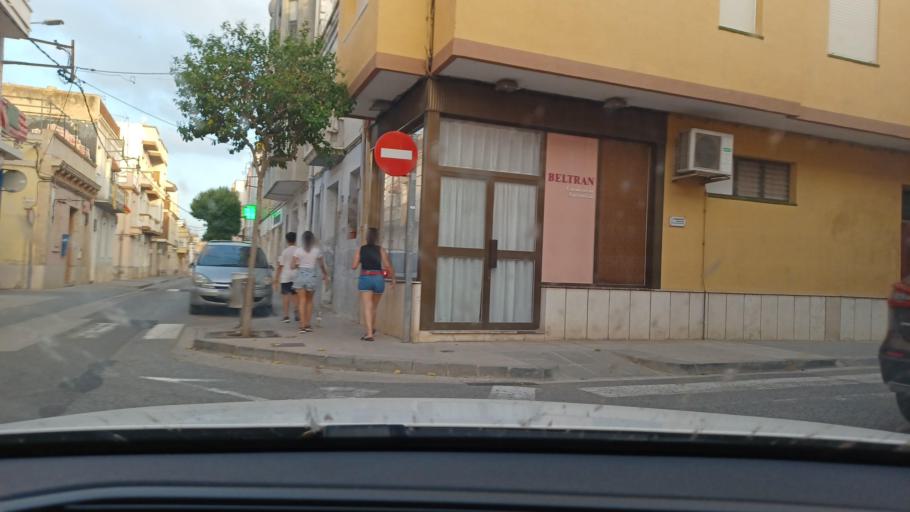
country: ES
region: Catalonia
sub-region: Provincia de Tarragona
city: Amposta
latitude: 40.7151
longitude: 0.5762
